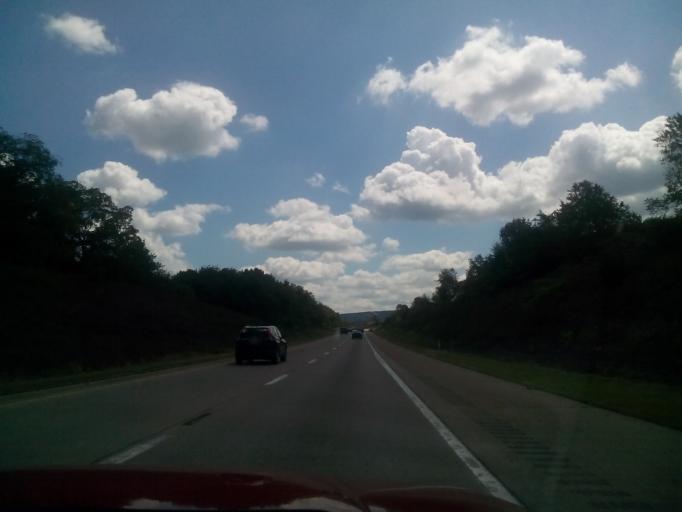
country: US
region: Pennsylvania
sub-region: Northumberland County
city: Milton
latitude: 40.9976
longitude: -76.7480
